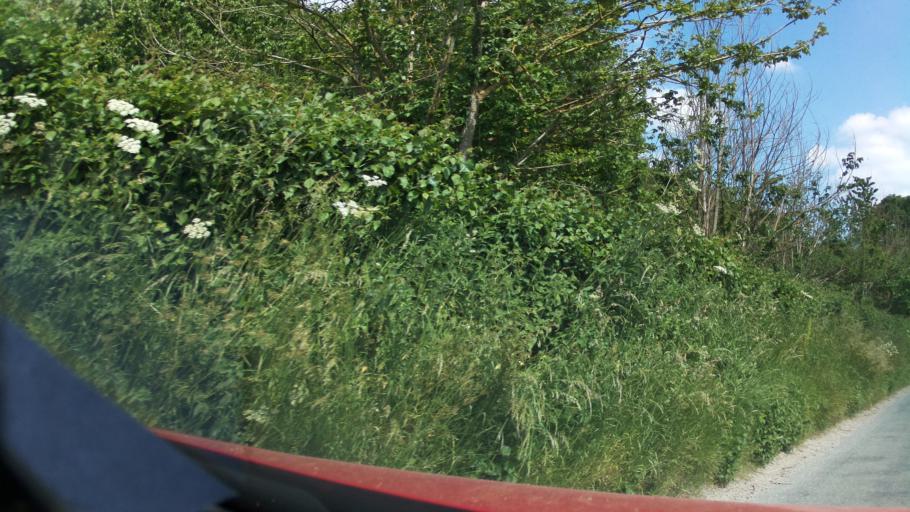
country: GB
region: England
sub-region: Wiltshire
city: Rushall
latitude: 51.2559
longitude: -1.7932
